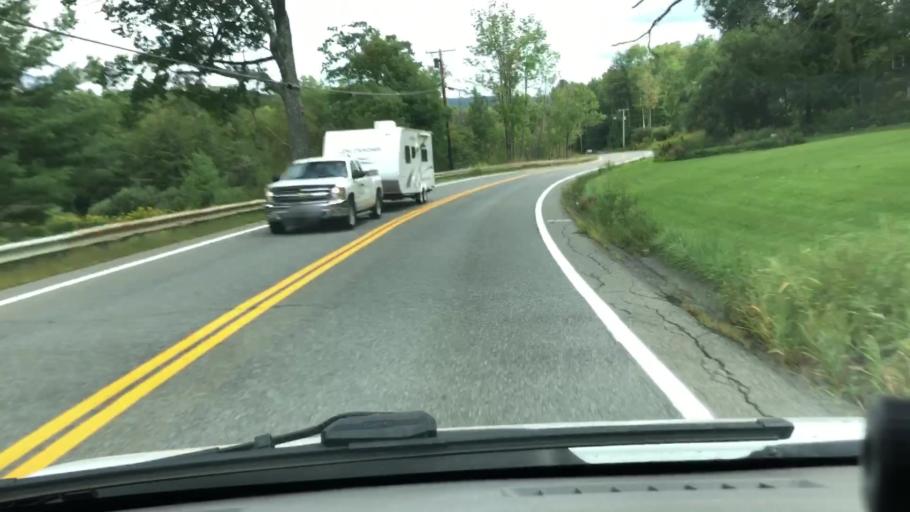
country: US
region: Massachusetts
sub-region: Berkshire County
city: North Adams
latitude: 42.6549
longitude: -72.9999
